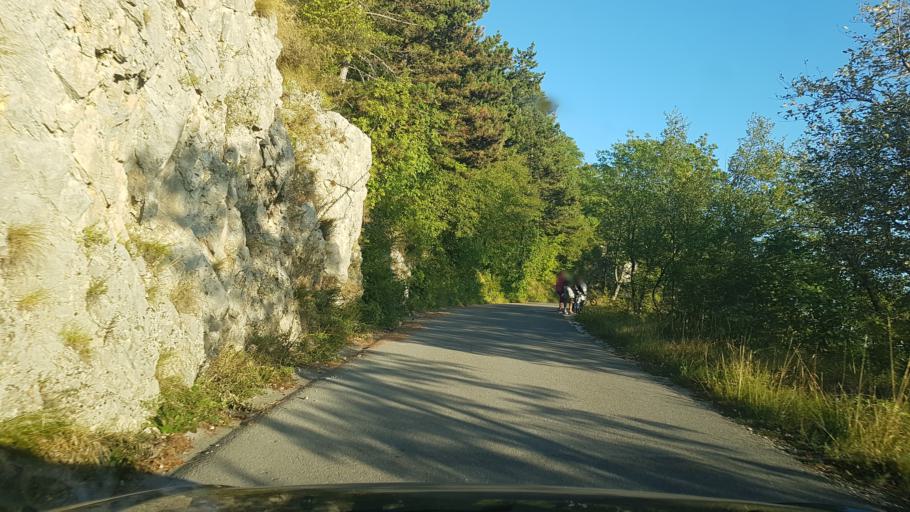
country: SI
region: Vipava
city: Vipava
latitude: 45.8010
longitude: 14.0019
